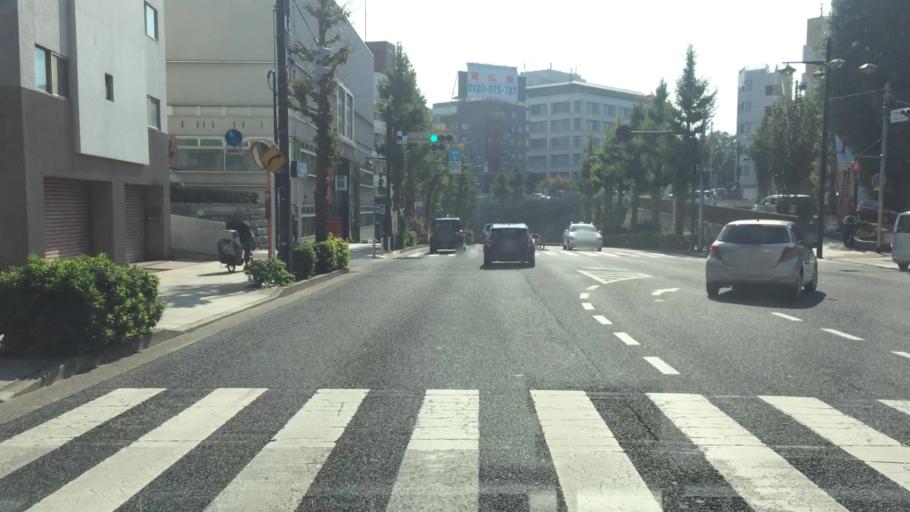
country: JP
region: Tokyo
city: Tokyo
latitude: 35.7202
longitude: 139.7132
